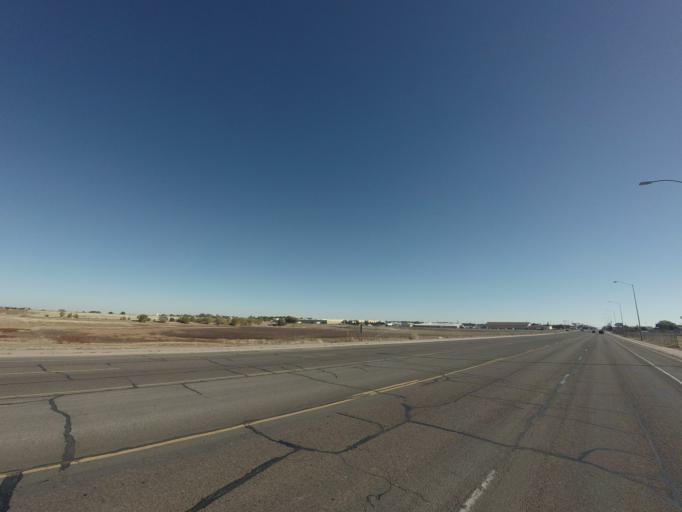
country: US
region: New Mexico
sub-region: Curry County
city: Clovis
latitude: 34.4339
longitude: -103.2050
